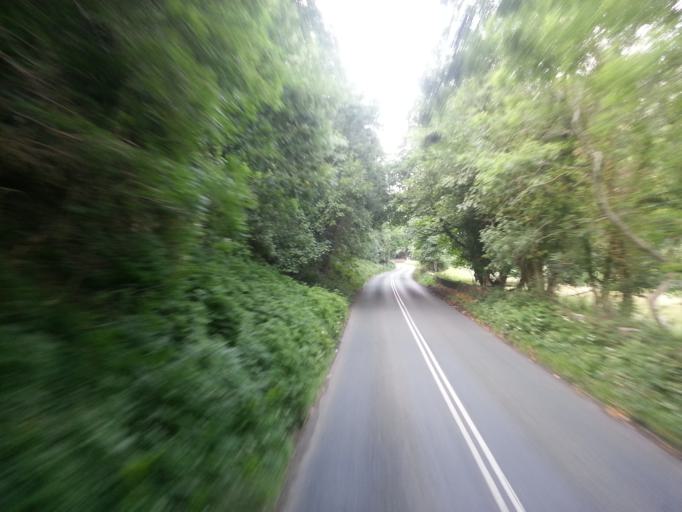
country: IE
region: Leinster
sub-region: Wicklow
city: Enniskerry
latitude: 53.2162
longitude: -6.1793
